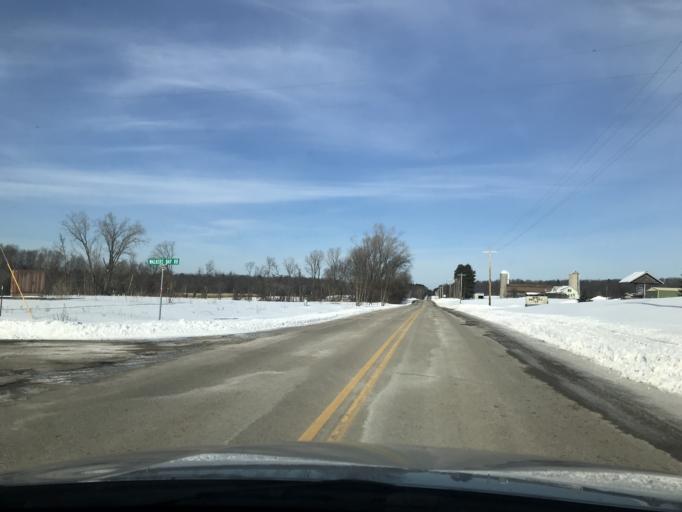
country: US
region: Wisconsin
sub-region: Oconto County
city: Oconto Falls
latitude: 45.1518
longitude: -88.1877
